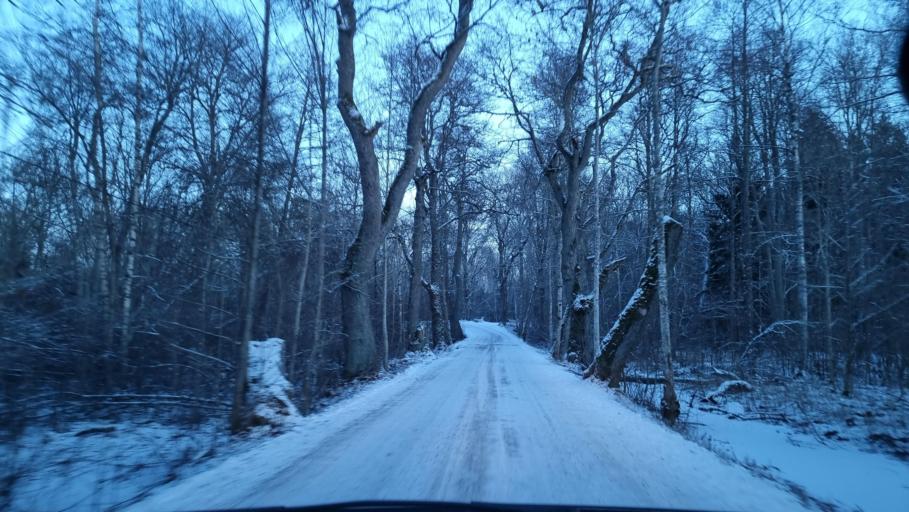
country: SE
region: Stockholm
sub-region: Vallentuna Kommun
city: Vallentuna
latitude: 59.5830
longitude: 18.1148
